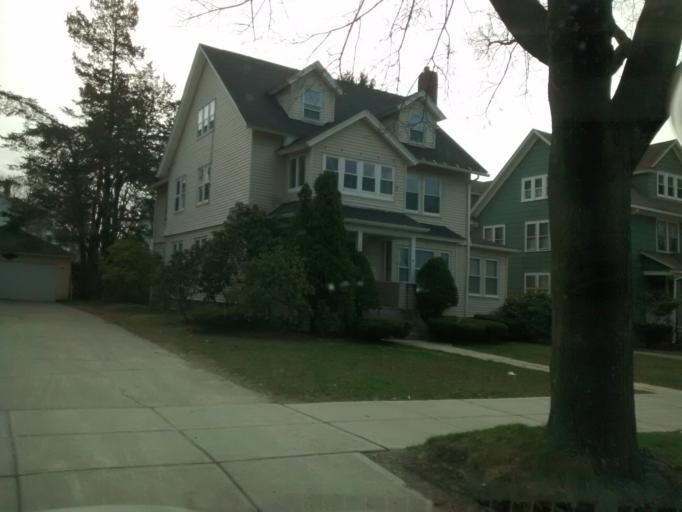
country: US
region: Massachusetts
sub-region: Worcester County
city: Worcester
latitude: 42.2698
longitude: -71.8147
